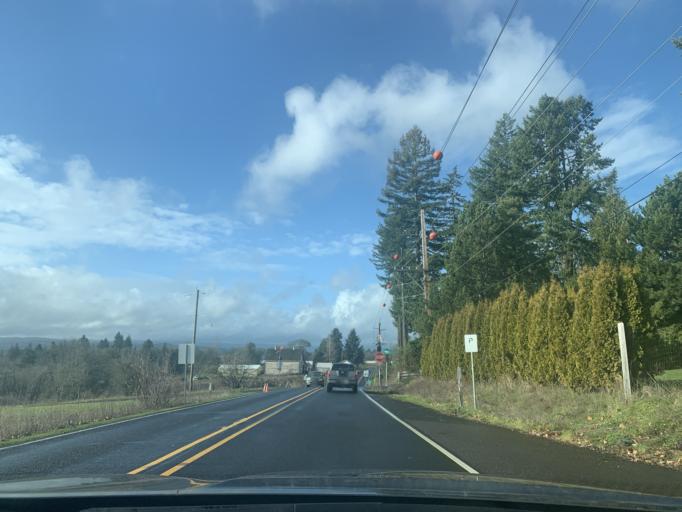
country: US
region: Oregon
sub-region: Washington County
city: King City
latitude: 45.4018
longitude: -122.8305
